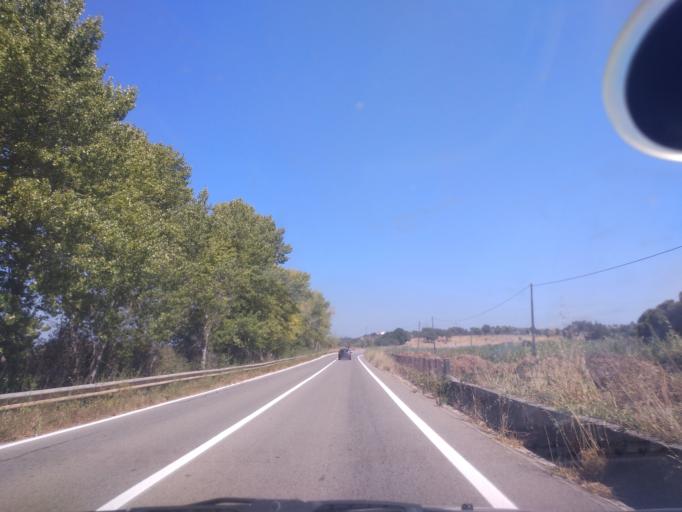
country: PT
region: Faro
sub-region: Lagos
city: Lagos
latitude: 37.1291
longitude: -8.6965
